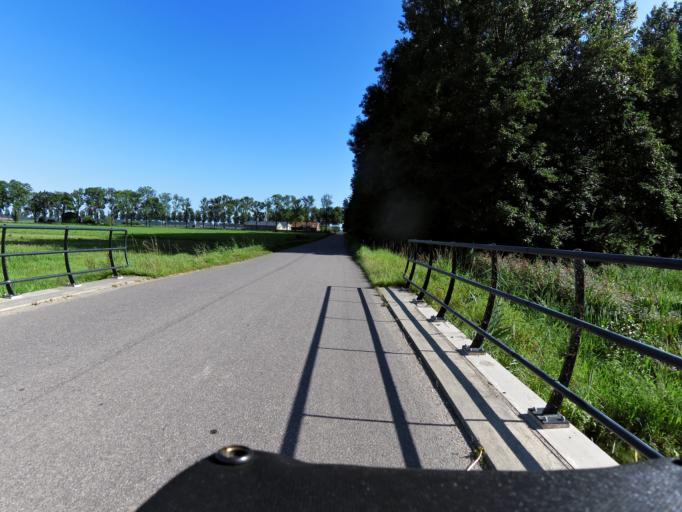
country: NL
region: South Holland
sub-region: Gemeente Dordrecht
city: Dordrecht
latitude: 51.7633
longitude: 4.6923
